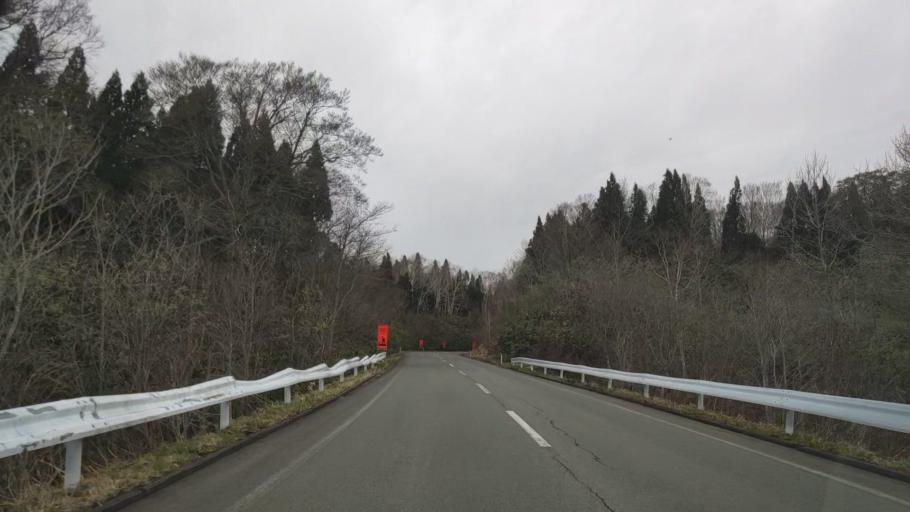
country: JP
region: Akita
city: Hanawa
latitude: 40.4109
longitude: 140.8478
